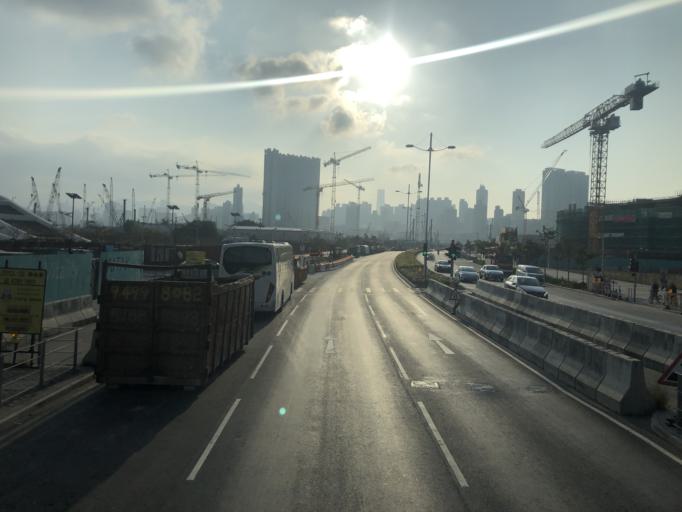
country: HK
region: Kowloon City
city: Kowloon
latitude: 22.3259
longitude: 114.2022
